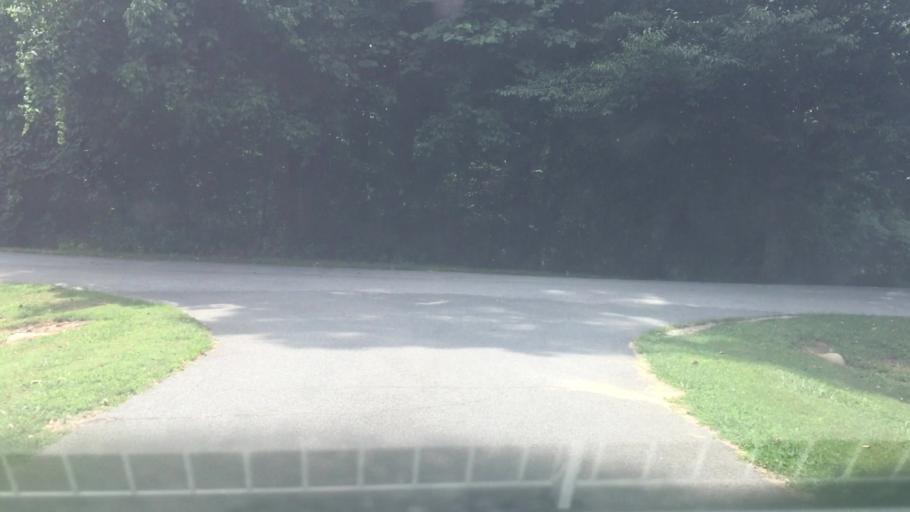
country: US
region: North Carolina
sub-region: Rowan County
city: China Grove
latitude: 35.6468
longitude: -80.6441
